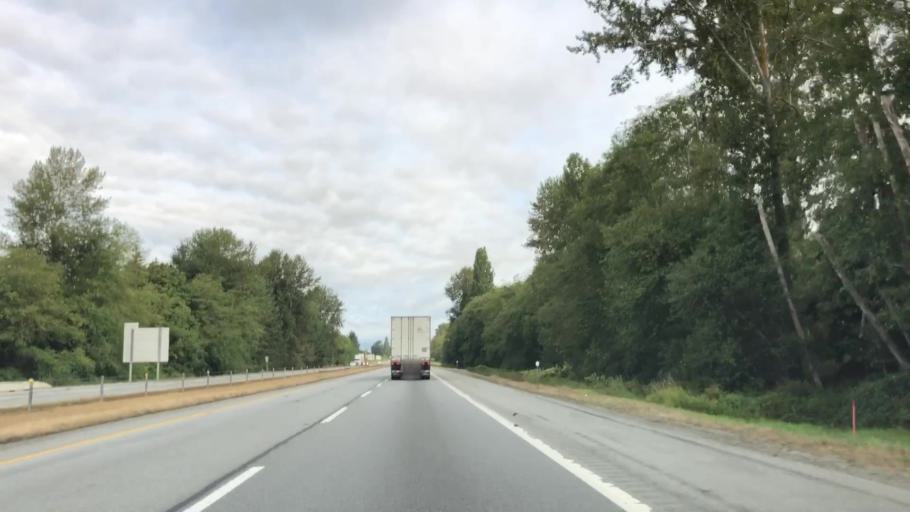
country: CA
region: British Columbia
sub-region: Greater Vancouver Regional District
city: White Rock
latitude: 49.0356
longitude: -122.7742
